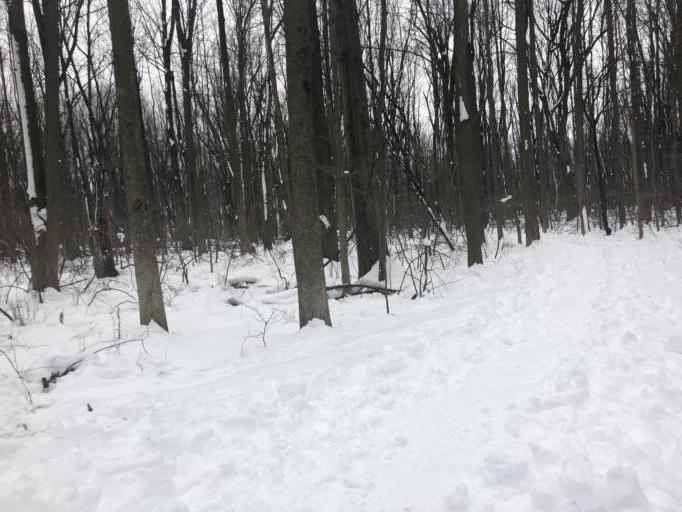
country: US
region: New York
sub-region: Monroe County
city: Pittsford
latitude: 43.0665
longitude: -77.5739
